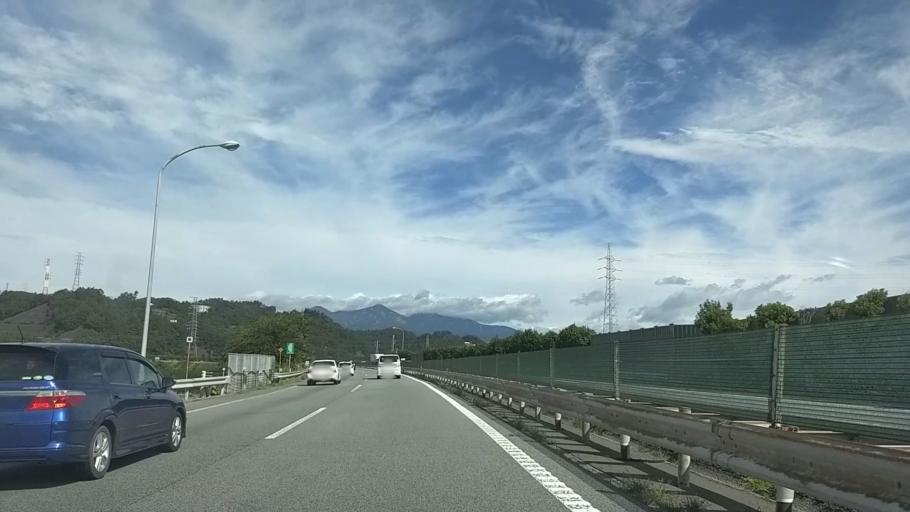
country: JP
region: Yamanashi
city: Nirasaki
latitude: 35.7797
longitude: 138.4222
